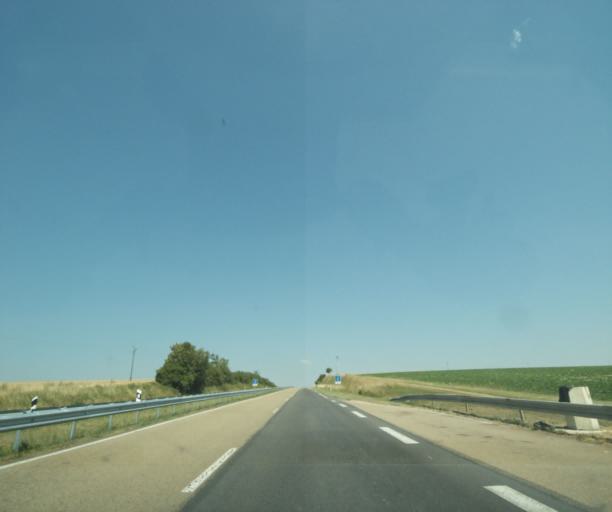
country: FR
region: Champagne-Ardenne
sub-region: Departement de la Marne
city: Fagnieres
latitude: 49.0510
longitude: 4.3036
